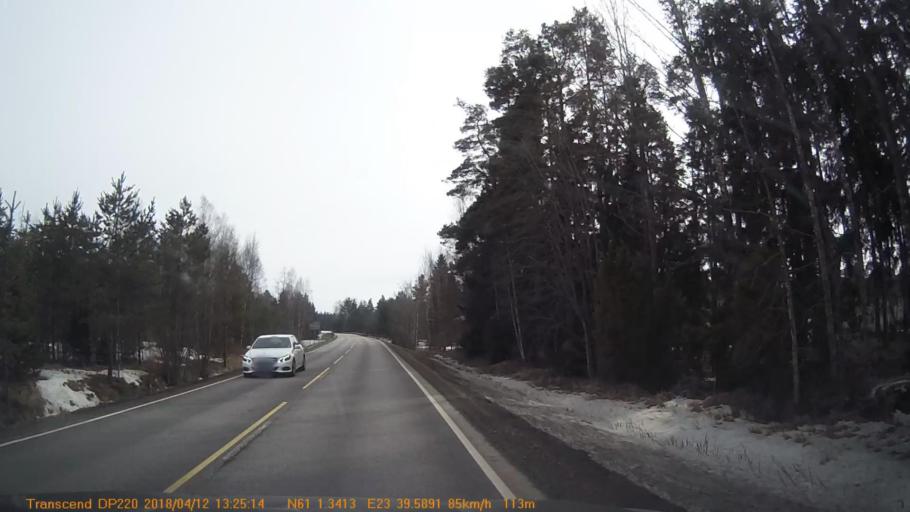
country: FI
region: Pirkanmaa
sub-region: Etelae-Pirkanmaa
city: Kylmaekoski
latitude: 61.0221
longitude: 23.6600
